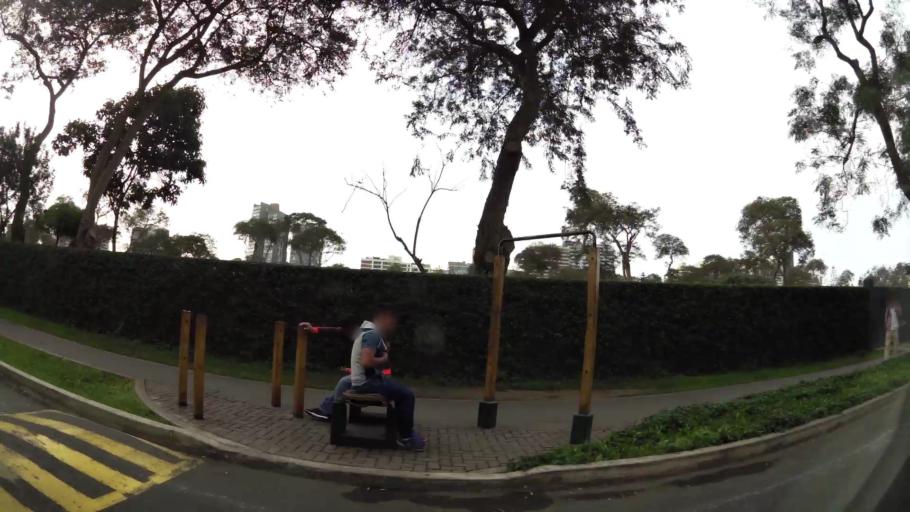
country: PE
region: Lima
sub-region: Lima
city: San Isidro
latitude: -12.1026
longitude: -77.0428
